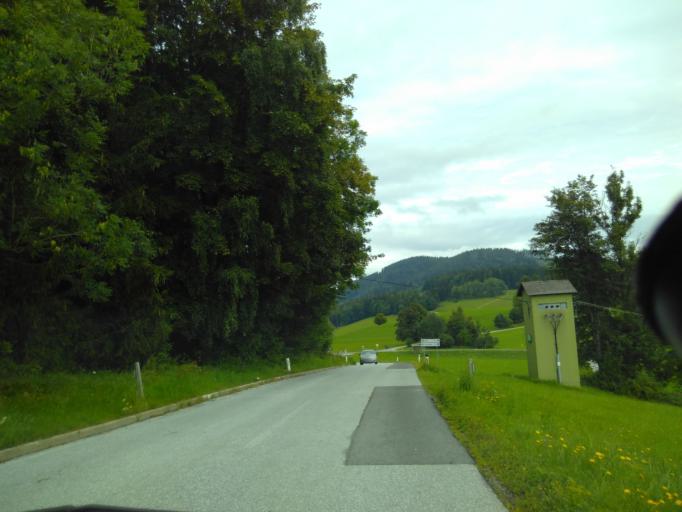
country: AT
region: Styria
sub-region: Politischer Bezirk Graz-Umgebung
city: Semriach
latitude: 47.2665
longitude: 15.4159
